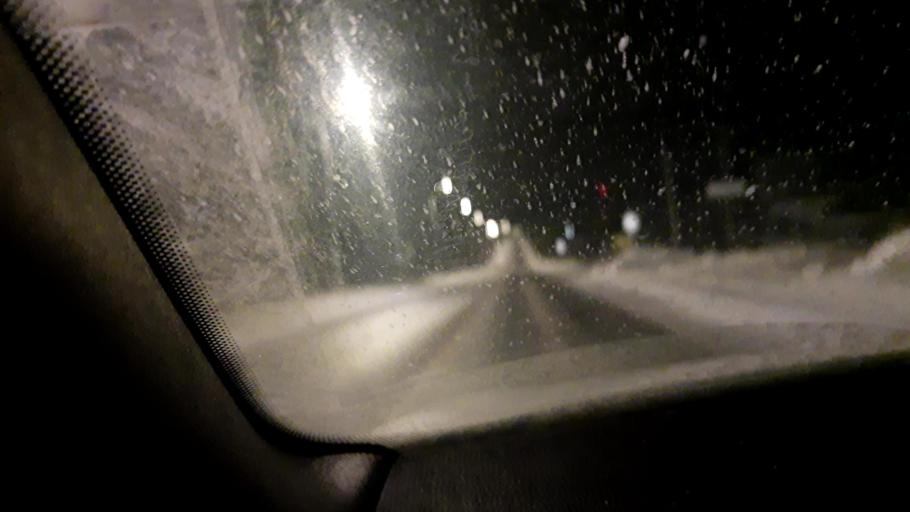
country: RU
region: Moskovskaya
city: Bogorodskoye
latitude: 56.5847
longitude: 38.1516
